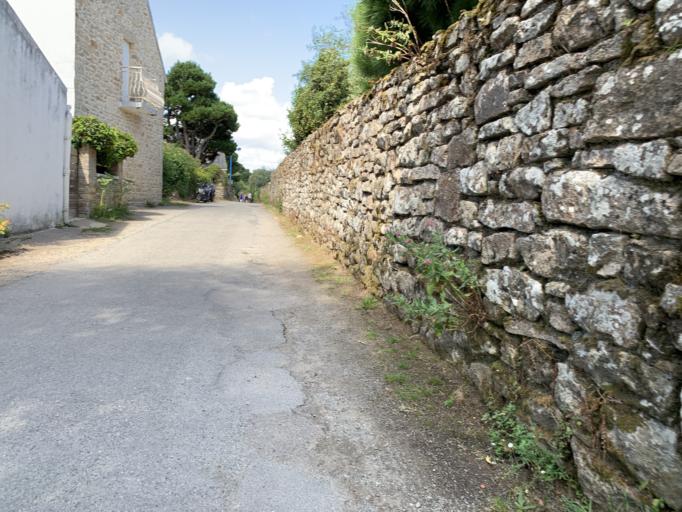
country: FR
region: Brittany
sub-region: Departement du Morbihan
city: Arradon
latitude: 47.5996
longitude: -2.8437
